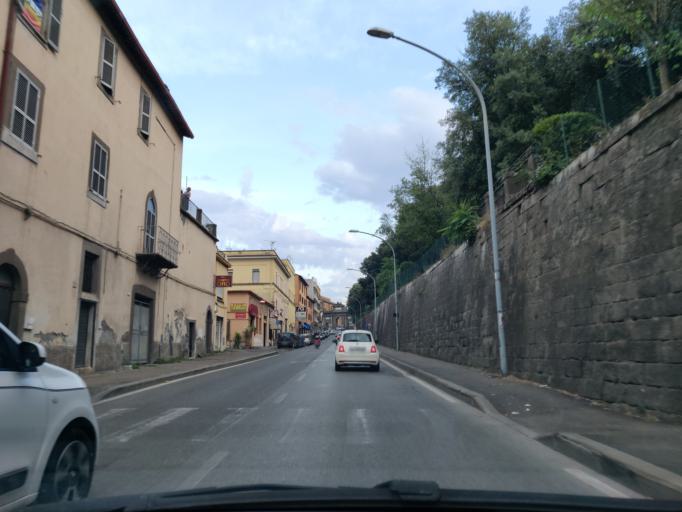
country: IT
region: Latium
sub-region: Provincia di Viterbo
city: Viterbo
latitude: 42.4239
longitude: 12.1019
